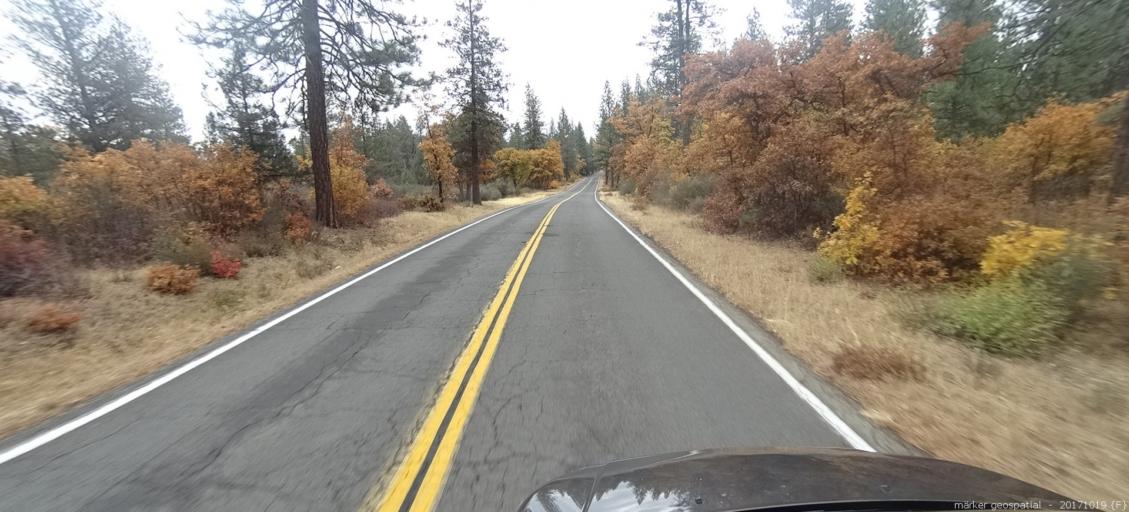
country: US
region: California
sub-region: Shasta County
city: Burney
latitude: 41.1449
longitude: -121.3485
